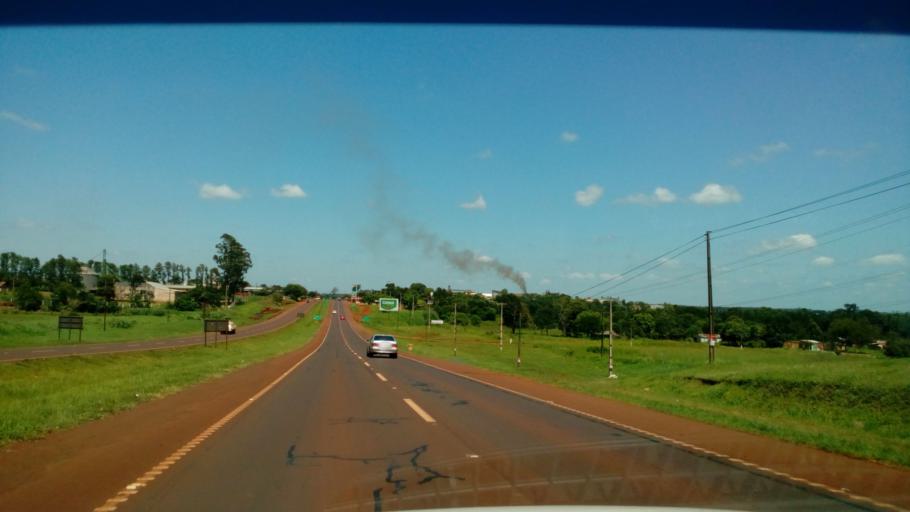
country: PY
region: Alto Parana
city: Colonia Yguazu
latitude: -25.4859
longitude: -54.8744
